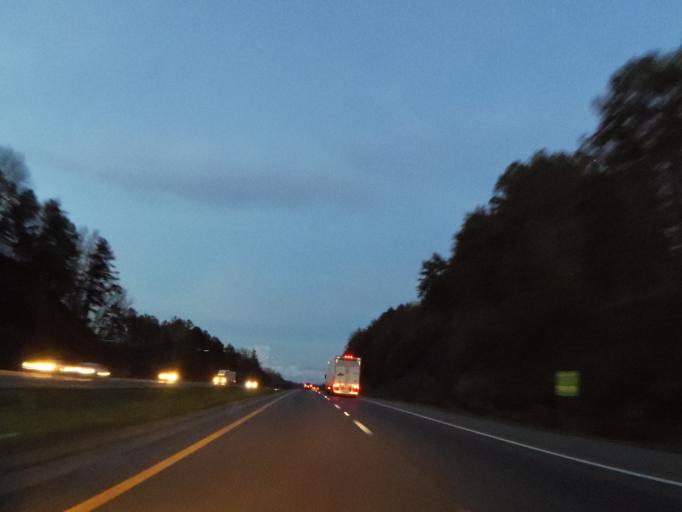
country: US
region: Kentucky
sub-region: Whitley County
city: Williamsburg
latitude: 36.8435
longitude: -84.1603
